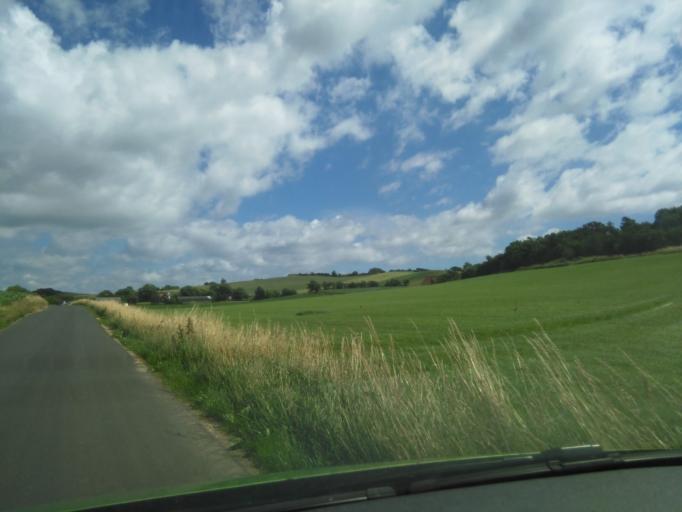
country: DK
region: Central Jutland
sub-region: Arhus Kommune
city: Logten
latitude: 56.1760
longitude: 10.3859
